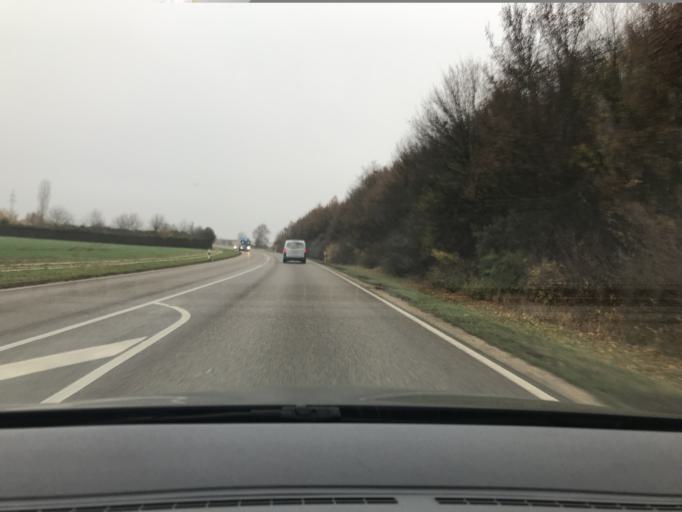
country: DE
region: Bavaria
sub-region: Swabia
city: Noerdlingen
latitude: 48.8626
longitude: 10.4712
